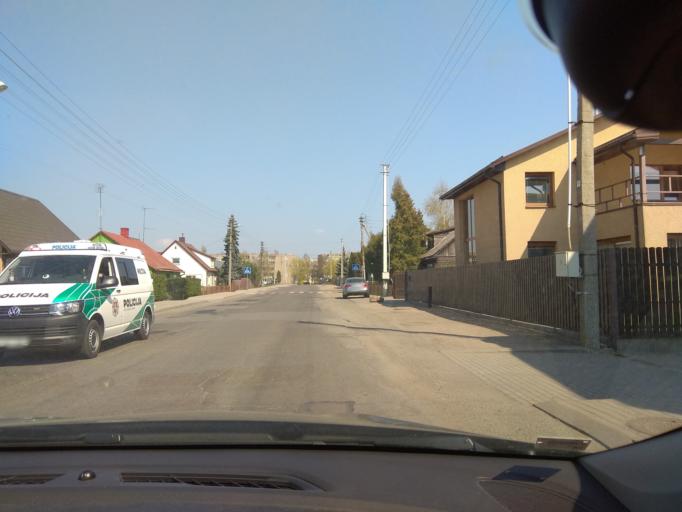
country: LT
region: Marijampoles apskritis
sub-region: Marijampole Municipality
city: Marijampole
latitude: 54.5653
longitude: 23.3502
